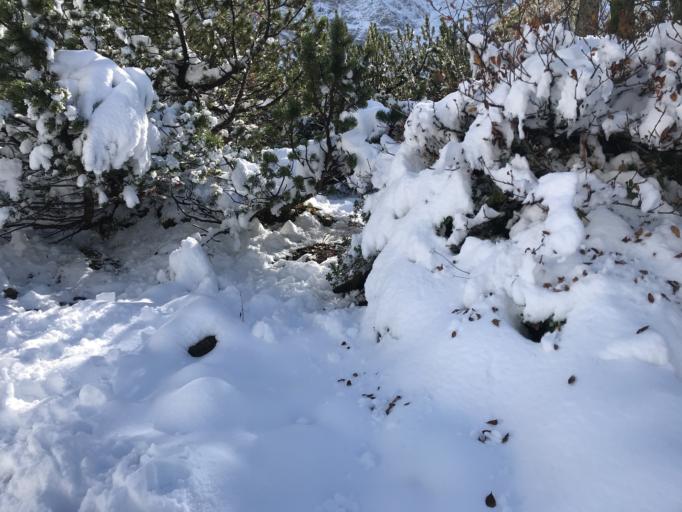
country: AT
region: Tyrol
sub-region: Politischer Bezirk Innsbruck Land
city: Gnadenwald
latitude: 47.3931
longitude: 11.5886
